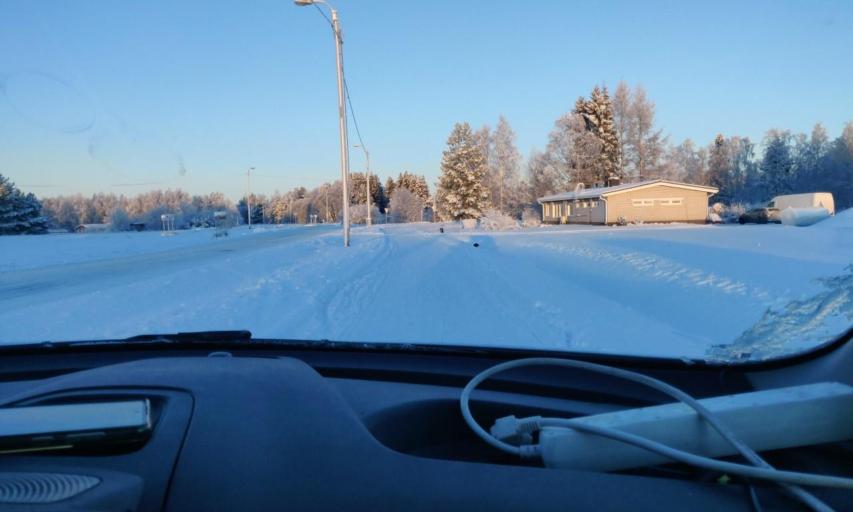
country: FI
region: Northern Ostrobothnia
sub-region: Raahe
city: Siikajoki
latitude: 64.8145
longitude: 24.7678
